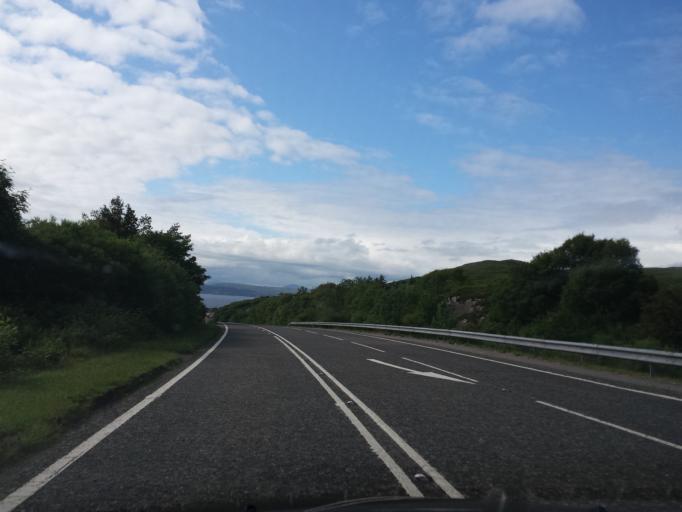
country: GB
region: Scotland
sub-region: Argyll and Bute
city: Isle Of Mull
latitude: 56.9897
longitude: -5.8260
